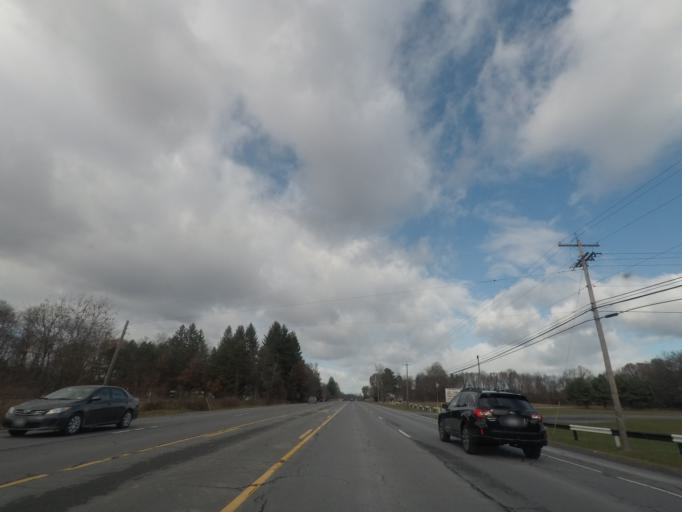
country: US
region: New York
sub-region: Saratoga County
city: Ballston Spa
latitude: 42.9881
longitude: -73.7879
